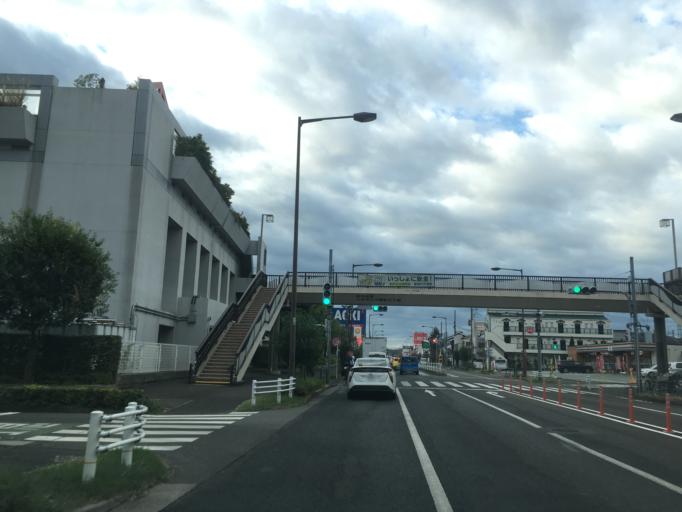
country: JP
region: Tokyo
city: Higashimurayama-shi
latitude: 35.7355
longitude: 139.4657
